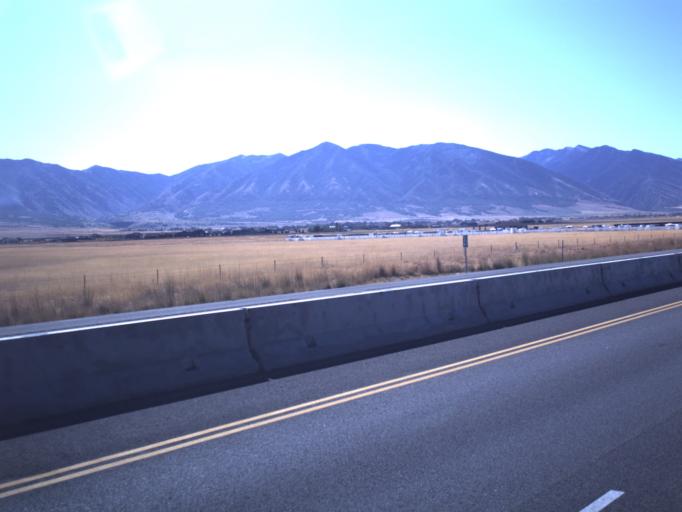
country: US
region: Utah
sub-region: Tooele County
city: Erda
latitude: 40.5988
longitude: -112.2942
